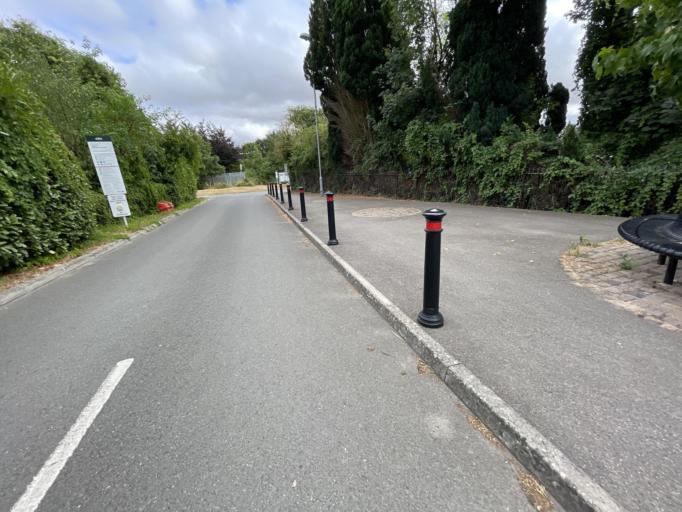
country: GB
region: England
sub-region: Oxfordshire
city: Radley
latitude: 51.6866
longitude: -1.2410
